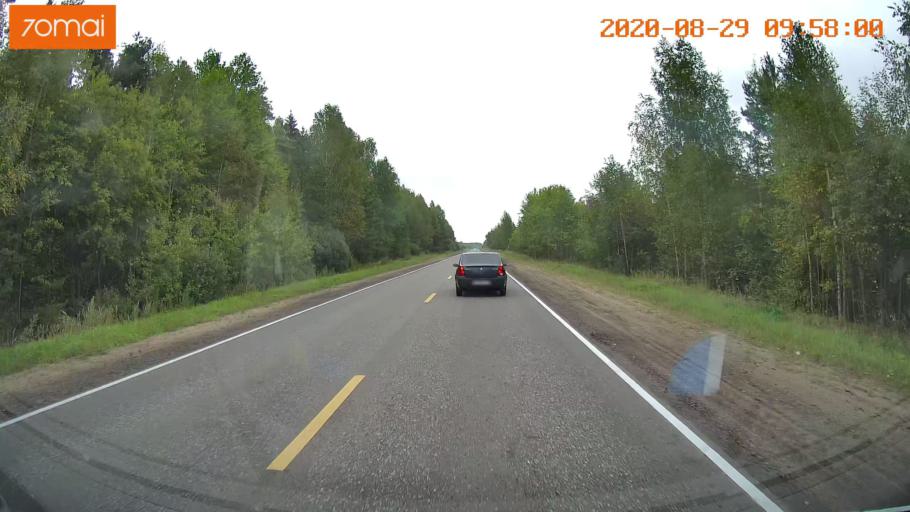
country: RU
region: Ivanovo
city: Zarechnyy
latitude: 57.4148
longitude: 42.3282
